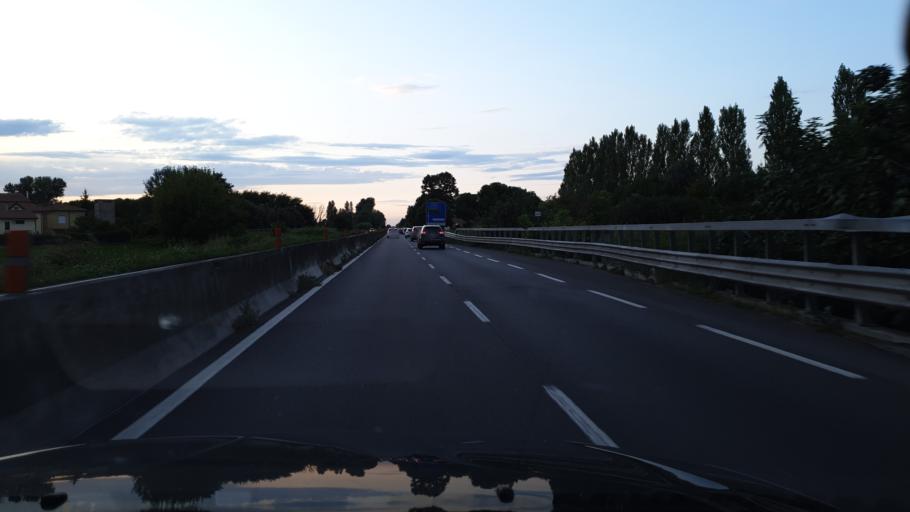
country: IT
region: Emilia-Romagna
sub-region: Provincia di Ravenna
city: Ravenna
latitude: 44.4024
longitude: 12.1786
